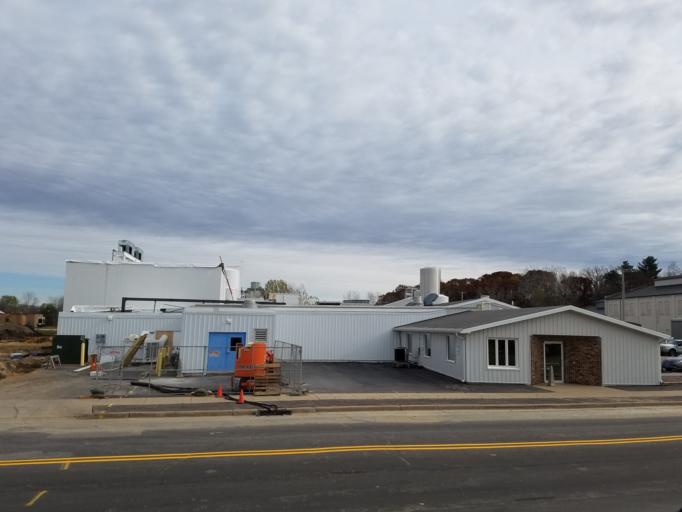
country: US
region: Wisconsin
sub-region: Vernon County
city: Hillsboro
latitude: 43.6526
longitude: -90.3349
